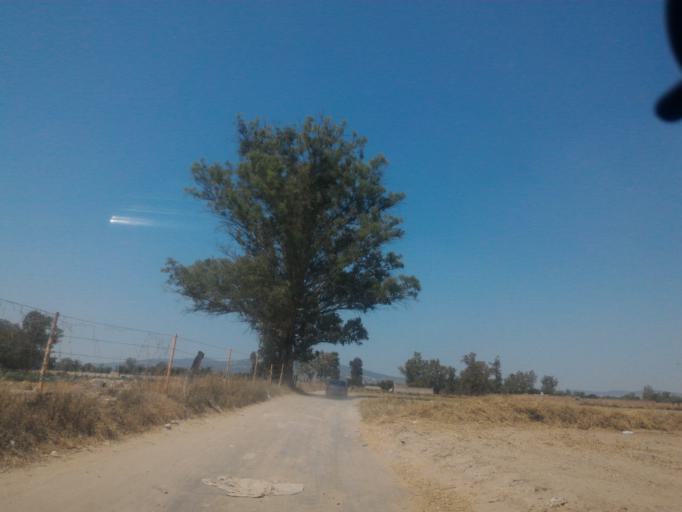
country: MX
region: Jalisco
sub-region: San Pedro Tlaquepaque
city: Paseo del Prado
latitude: 20.5623
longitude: -103.3959
